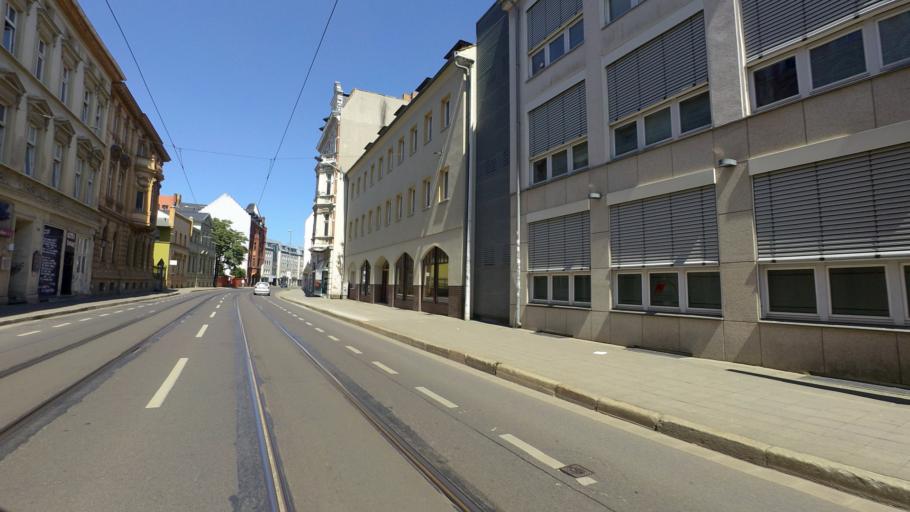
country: DE
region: Brandenburg
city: Cottbus
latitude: 51.7549
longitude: 14.3332
